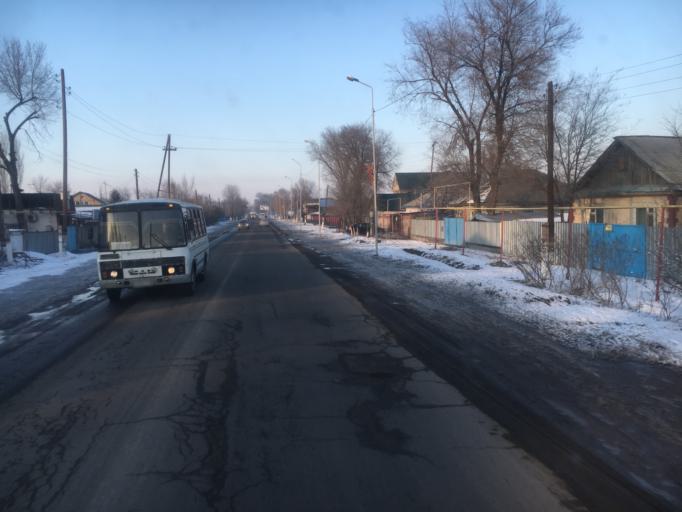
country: KZ
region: Almaty Oblysy
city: Burunday
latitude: 43.3713
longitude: 76.6416
